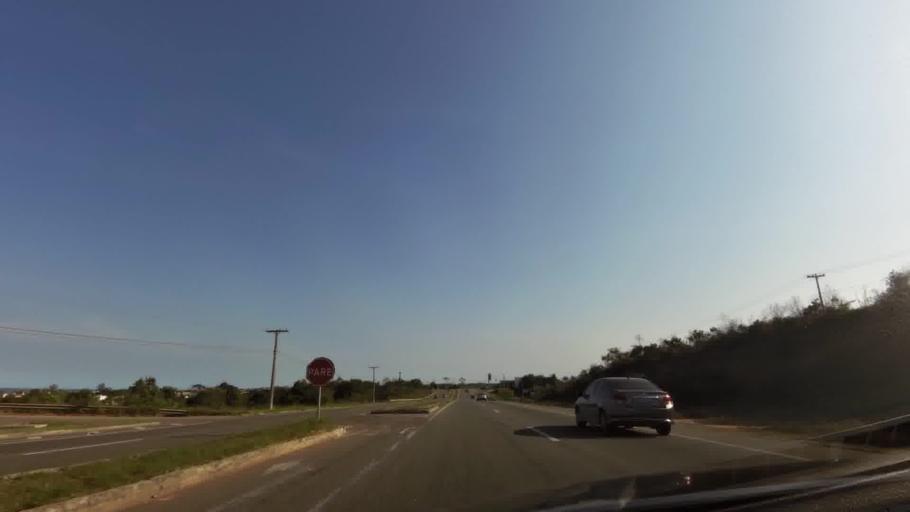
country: BR
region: Espirito Santo
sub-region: Vitoria
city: Vitoria
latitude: -20.4660
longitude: -40.3479
